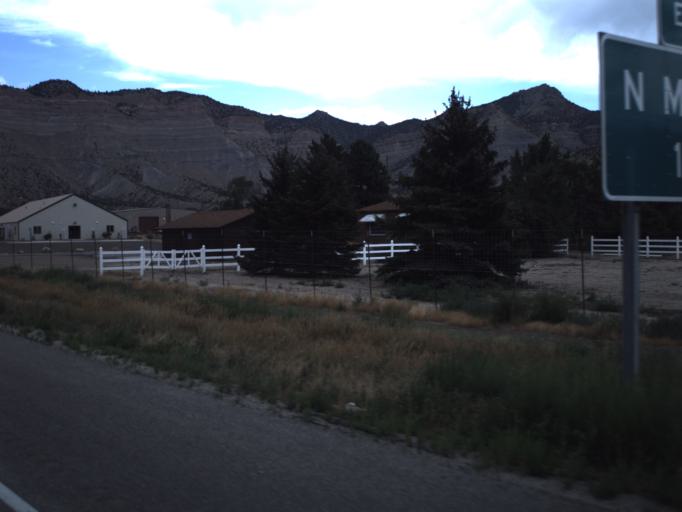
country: US
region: Utah
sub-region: Carbon County
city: Helper
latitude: 39.6750
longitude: -110.8615
